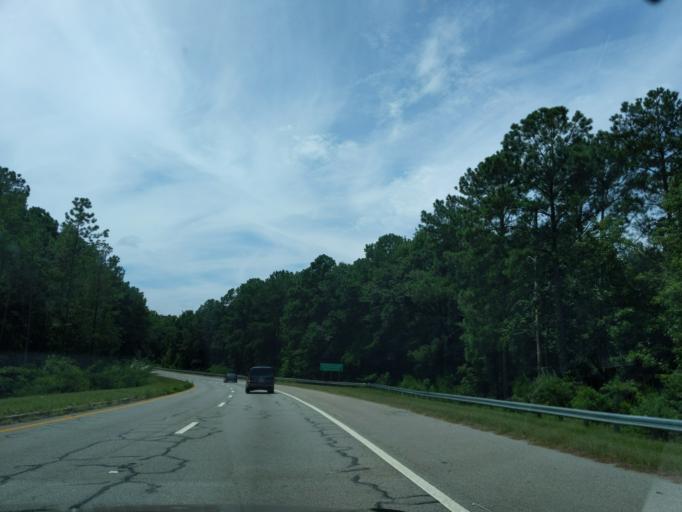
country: US
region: South Carolina
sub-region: Richland County
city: Columbia
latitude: 34.0286
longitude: -81.0368
